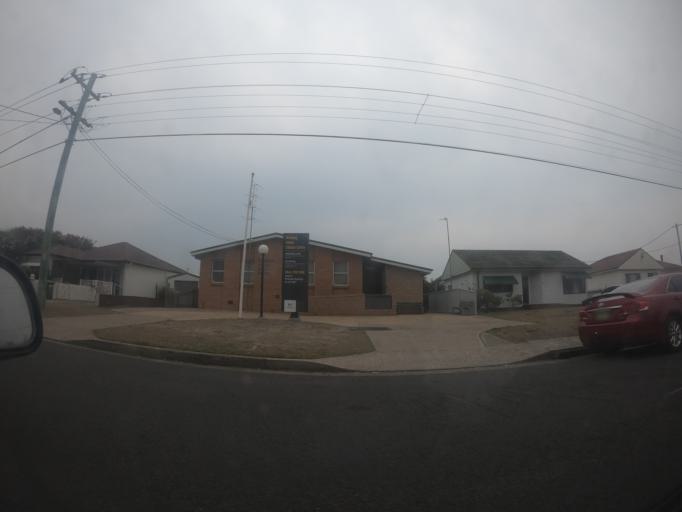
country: AU
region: New South Wales
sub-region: Shellharbour
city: Lake Illawarra
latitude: -34.5287
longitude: 150.8703
